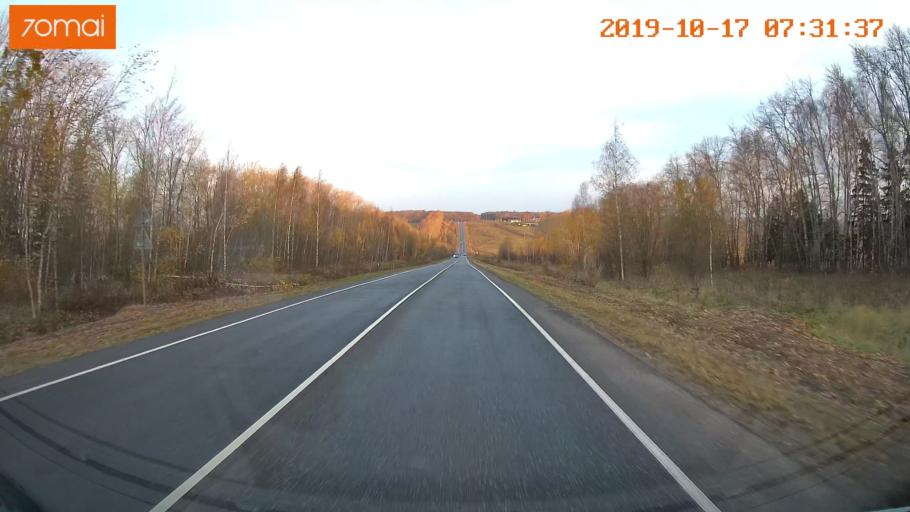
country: RU
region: Ivanovo
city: Gavrilov Posad
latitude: 56.3910
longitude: 39.9926
